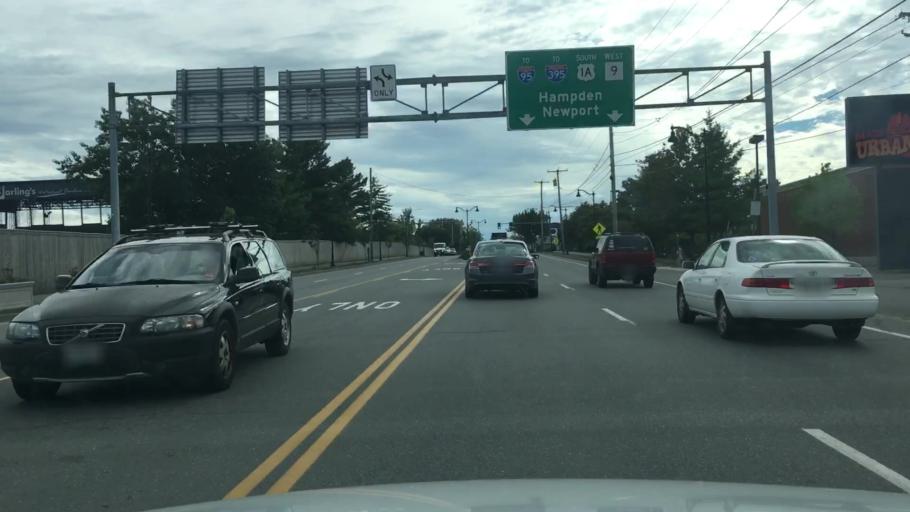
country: US
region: Maine
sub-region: Penobscot County
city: Bangor
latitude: 44.7946
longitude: -68.7748
